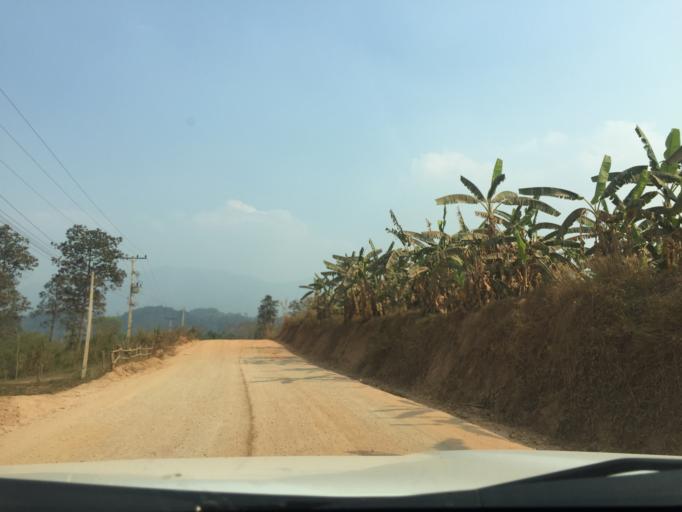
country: LA
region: Xiagnabouli
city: Sainyabuli
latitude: 19.2155
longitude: 101.6899
